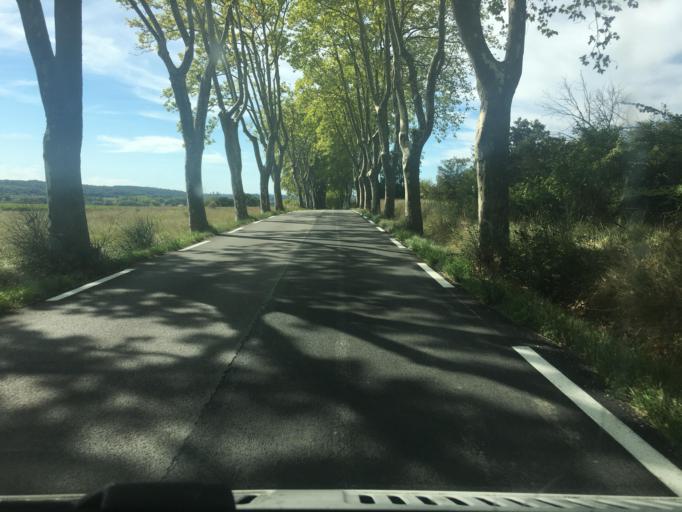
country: FR
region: Languedoc-Roussillon
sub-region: Departement du Gard
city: Saint-Quentin-la-Poterie
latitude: 44.0317
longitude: 4.4847
